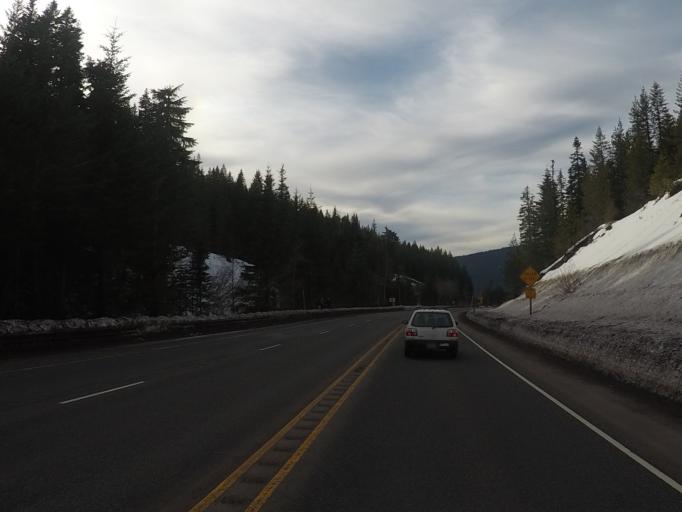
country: US
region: Oregon
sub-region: Clackamas County
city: Mount Hood Village
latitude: 45.3046
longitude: -121.7862
